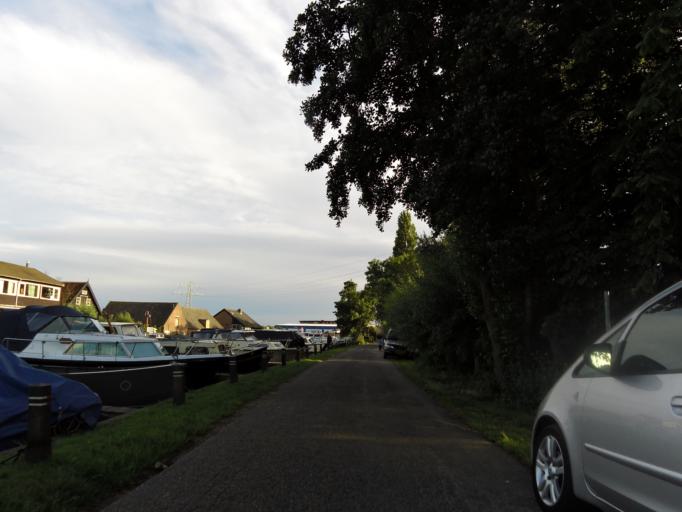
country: NL
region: South Holland
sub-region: Gemeente Oegstgeest
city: Oegstgeest
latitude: 52.1844
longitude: 4.4907
